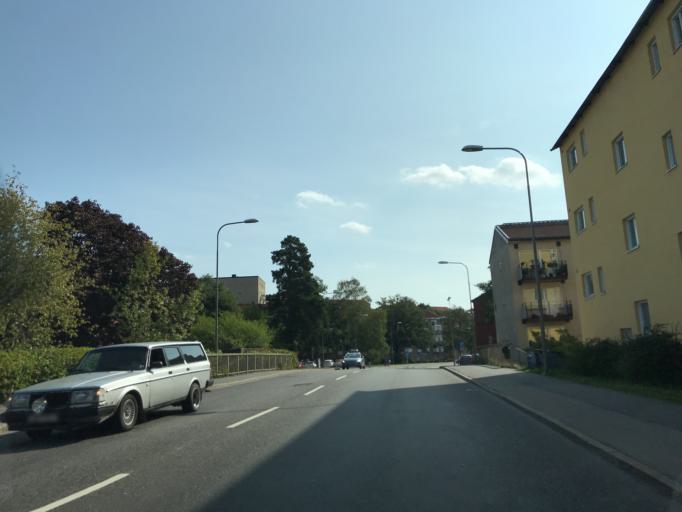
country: SE
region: Stockholm
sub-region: Huddinge Kommun
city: Segeltorp
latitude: 59.2849
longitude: 17.9664
